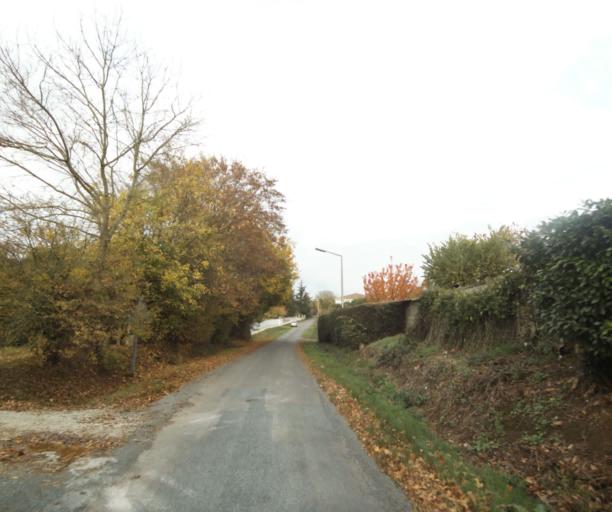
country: FR
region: Poitou-Charentes
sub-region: Departement de la Charente-Maritime
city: Saint-Georges-des-Coteaux
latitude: 45.7700
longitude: -0.7180
